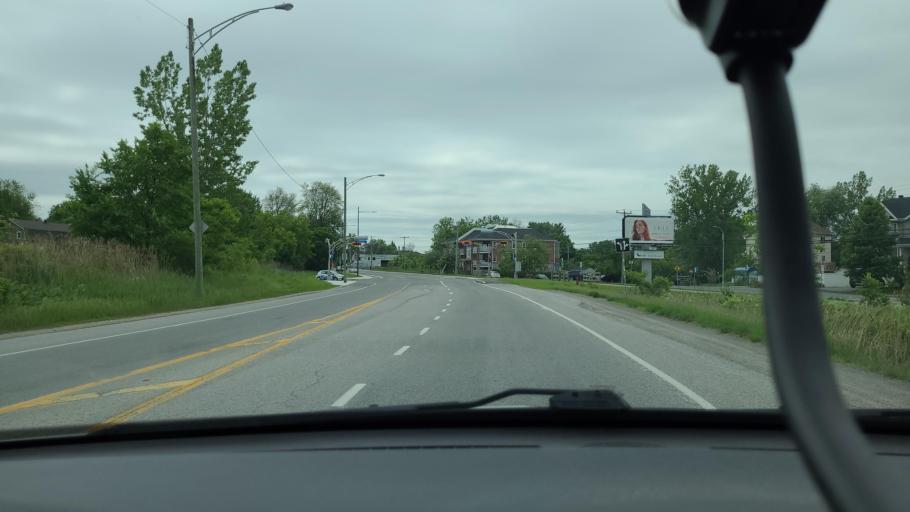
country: CA
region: Quebec
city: Bois-des-Filion
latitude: 45.6539
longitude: -73.7478
